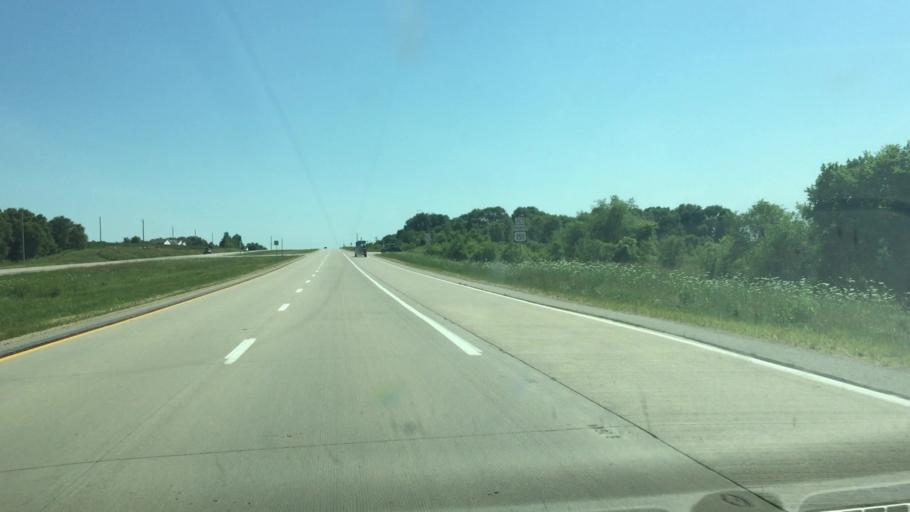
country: US
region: Iowa
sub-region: Jones County
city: Monticello
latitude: 42.2579
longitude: -91.1556
